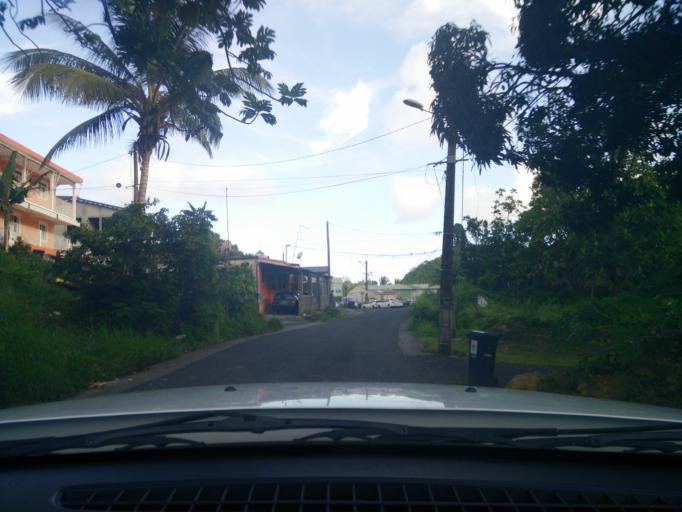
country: GP
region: Guadeloupe
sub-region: Guadeloupe
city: Les Abymes
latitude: 16.2522
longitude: -61.4991
